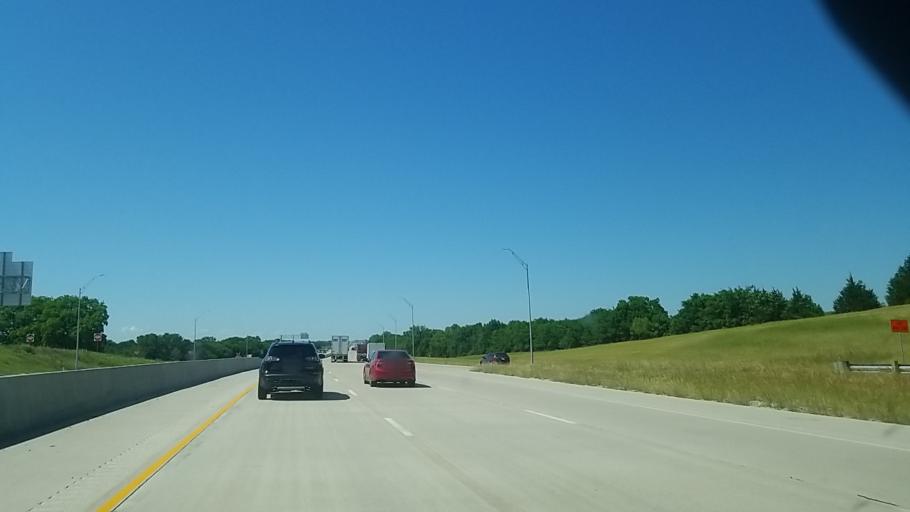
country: US
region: Texas
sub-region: Navarro County
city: Corsicana
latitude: 32.1534
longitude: -96.4679
